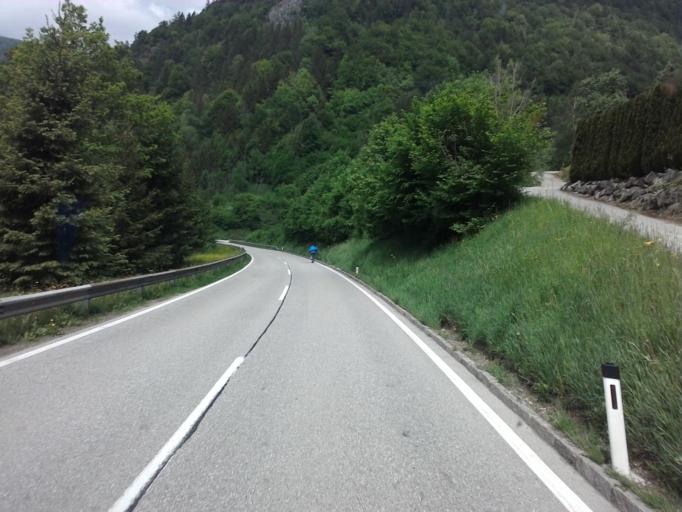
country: AT
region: Upper Austria
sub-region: Politischer Bezirk Steyr-Land
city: Maria Neustift
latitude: 47.8772
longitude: 14.6031
